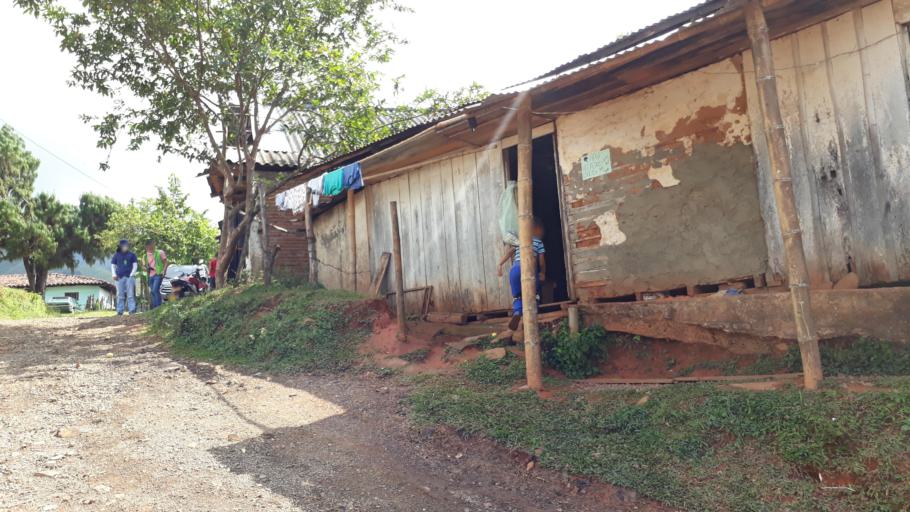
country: CO
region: Valle del Cauca
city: Jamundi
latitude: 3.2689
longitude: -76.6258
